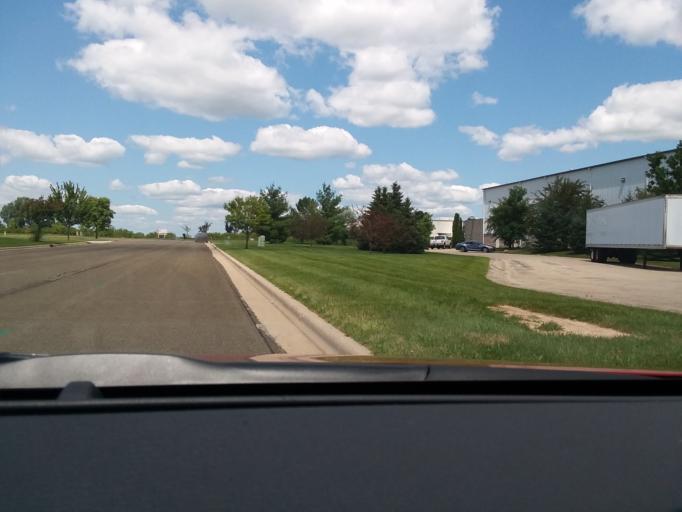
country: US
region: Wisconsin
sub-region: Dane County
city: Windsor
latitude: 43.2028
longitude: -89.3356
